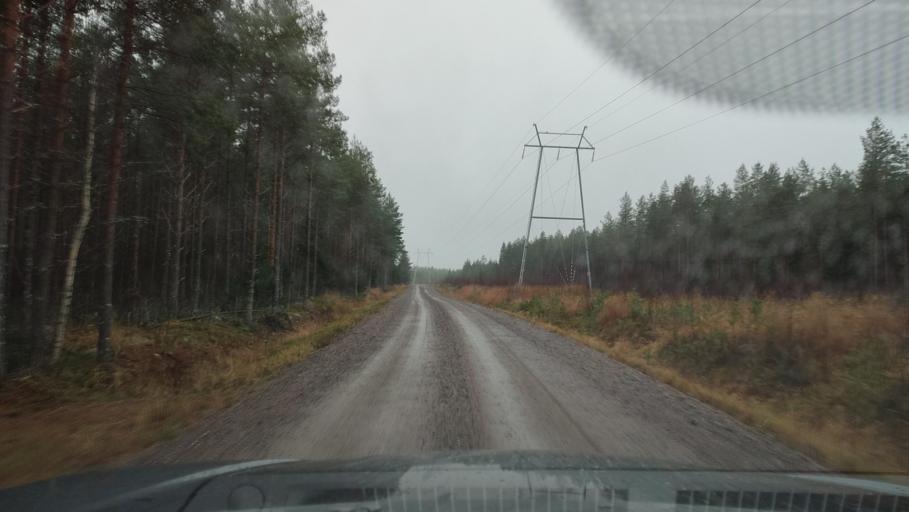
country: FI
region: Southern Ostrobothnia
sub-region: Suupohja
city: Karijoki
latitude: 62.2159
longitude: 21.7332
